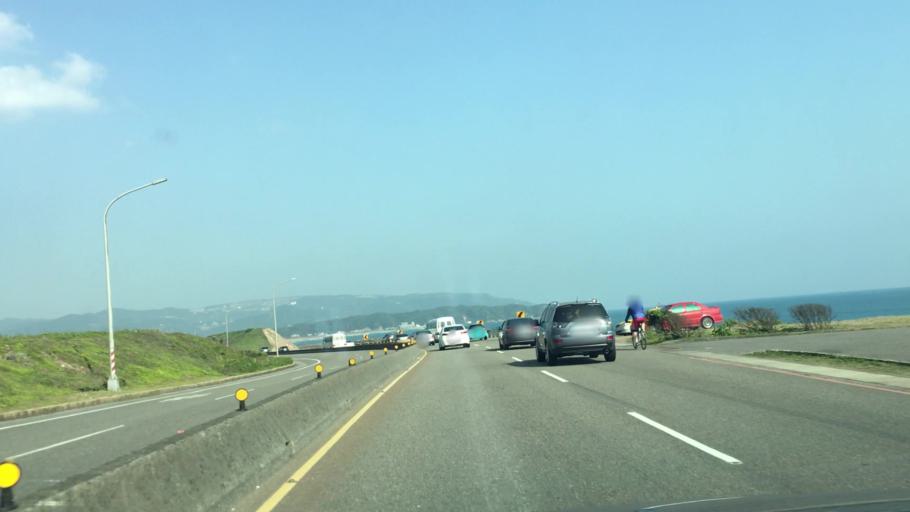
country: TW
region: Taiwan
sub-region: Keelung
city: Keelung
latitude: 25.2018
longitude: 121.6708
